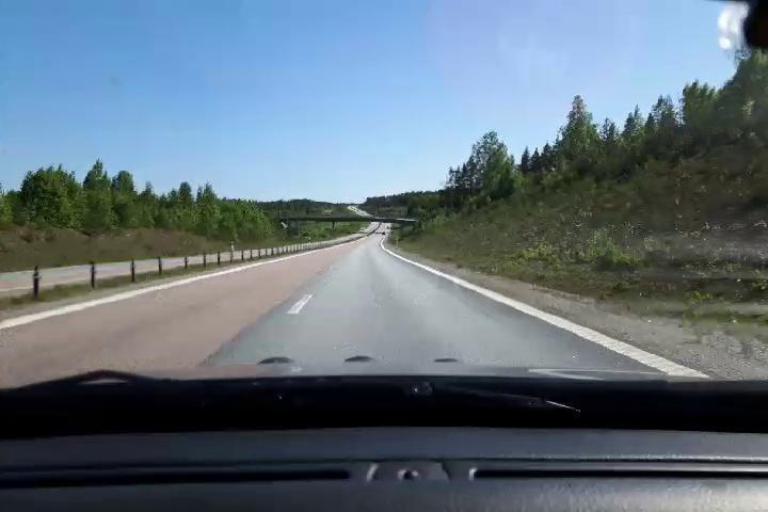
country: SE
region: Gaevleborg
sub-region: Soderhamns Kommun
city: Soderhamn
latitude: 61.3606
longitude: 17.0139
